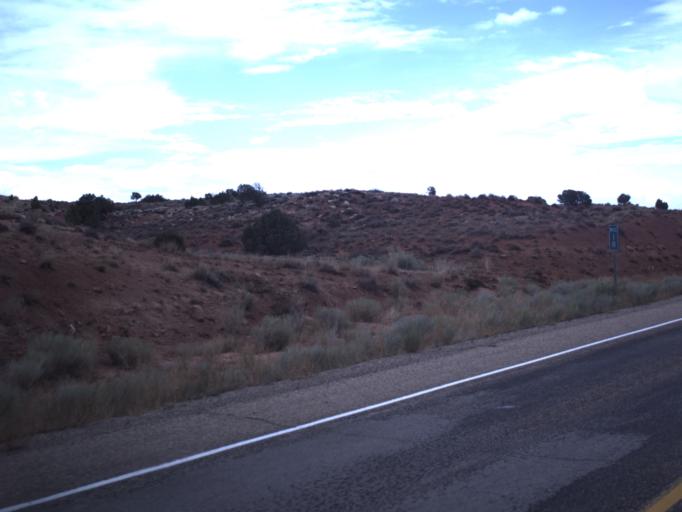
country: US
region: Utah
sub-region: Uintah County
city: Naples
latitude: 40.1643
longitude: -109.3133
